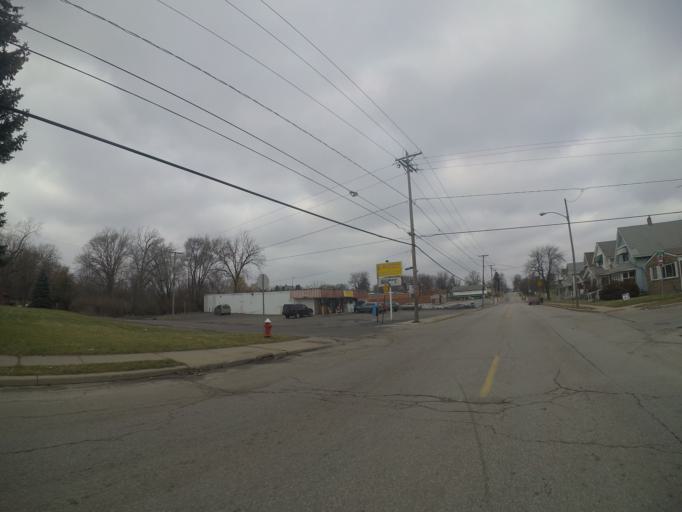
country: US
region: Ohio
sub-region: Lucas County
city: Oregon
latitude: 41.6279
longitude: -83.5154
